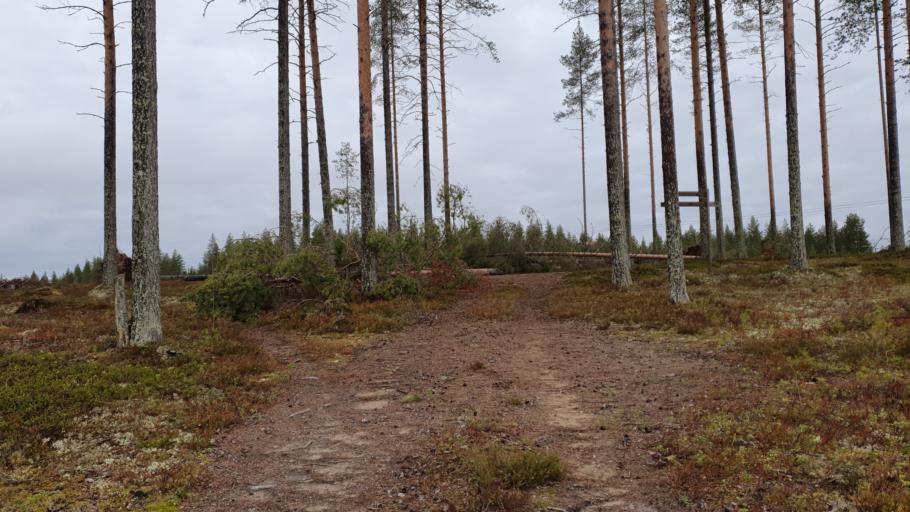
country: FI
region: Kainuu
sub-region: Kehys-Kainuu
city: Kuhmo
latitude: 64.1465
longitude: 29.4182
